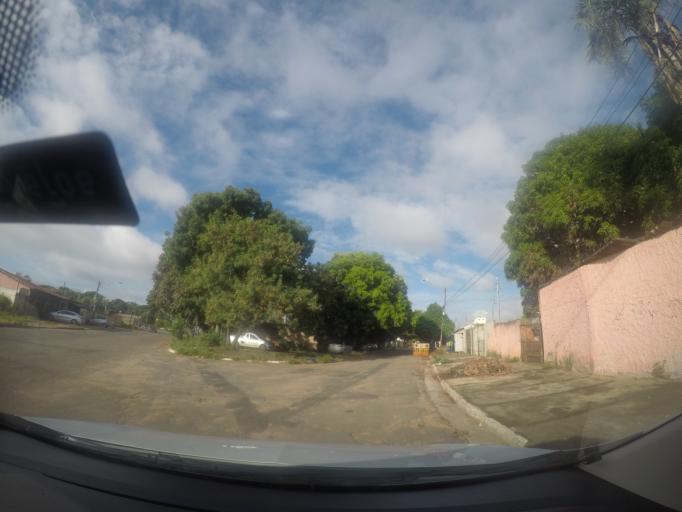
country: BR
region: Goias
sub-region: Goiania
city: Goiania
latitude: -16.6873
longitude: -49.3092
